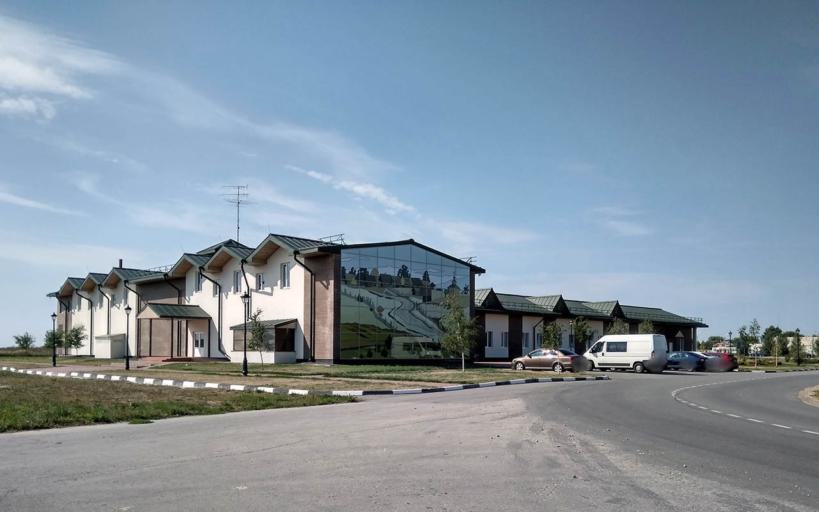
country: RU
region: Rjazan
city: Rybnoye
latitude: 54.8617
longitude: 39.6070
